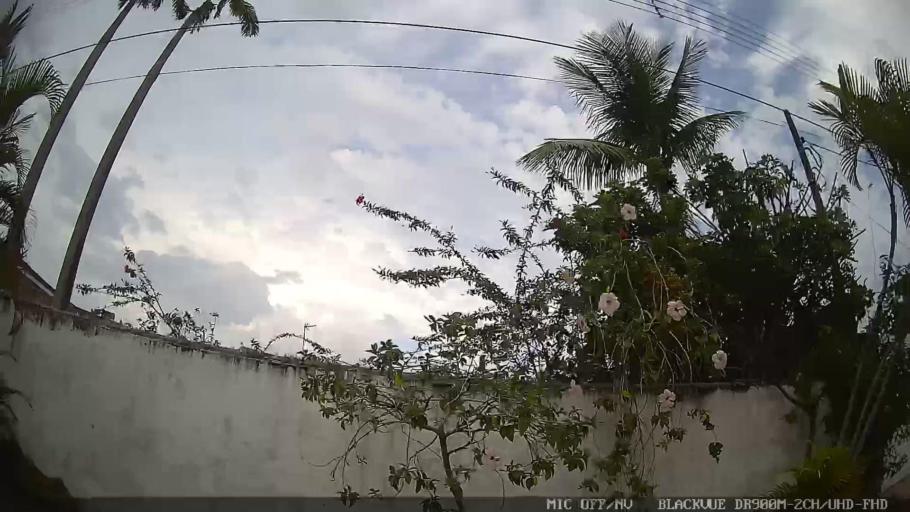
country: BR
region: Sao Paulo
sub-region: Guaruja
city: Guaruja
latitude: -23.9850
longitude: -46.2275
